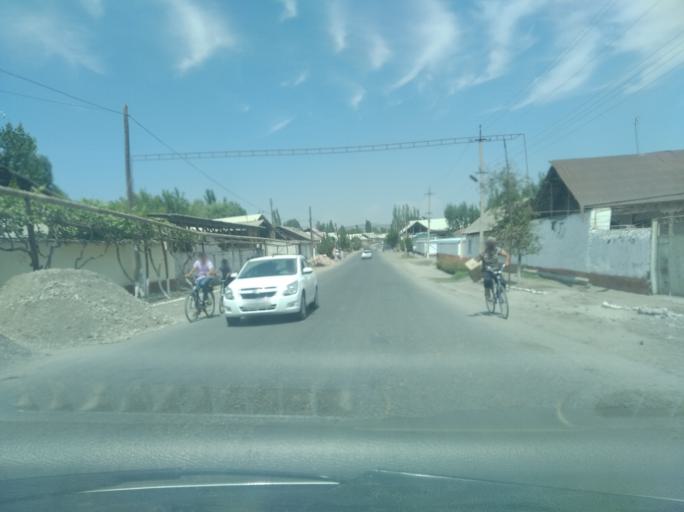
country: KG
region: Osh
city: Aravan
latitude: 40.6210
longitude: 72.4522
